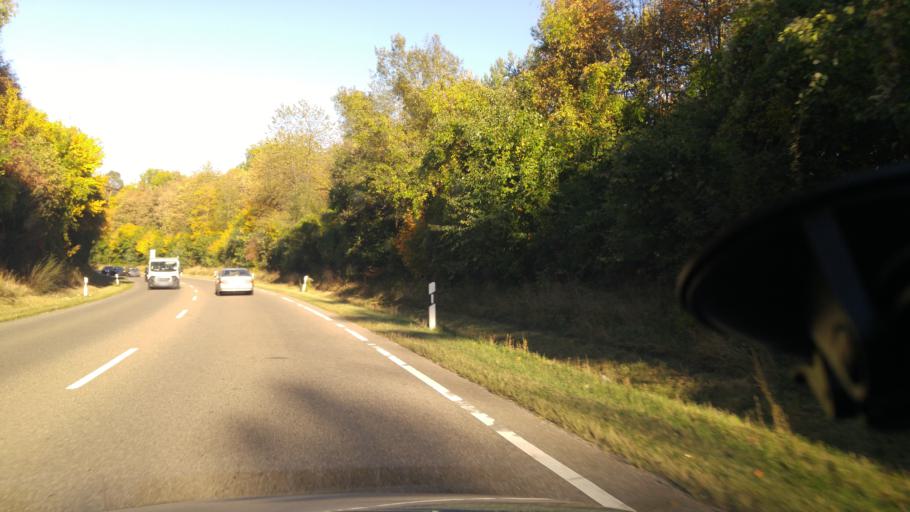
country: DE
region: Baden-Wuerttemberg
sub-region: Regierungsbezirk Stuttgart
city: Korntal
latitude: 48.8071
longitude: 9.1263
